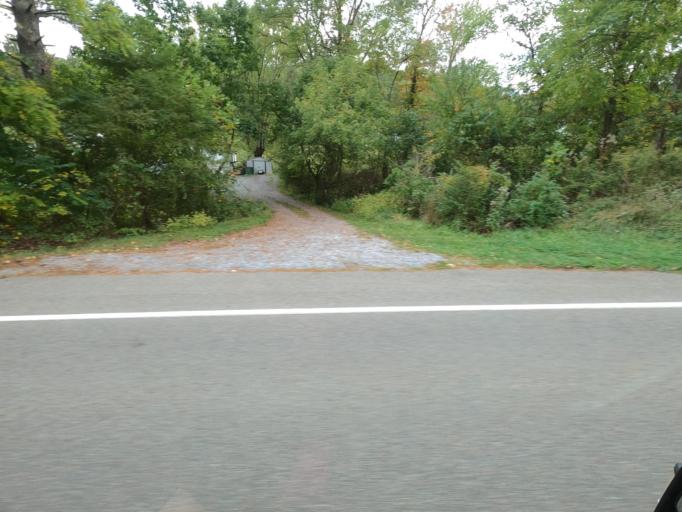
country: US
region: Tennessee
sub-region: Carter County
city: Elizabethton
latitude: 36.2630
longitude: -82.2014
